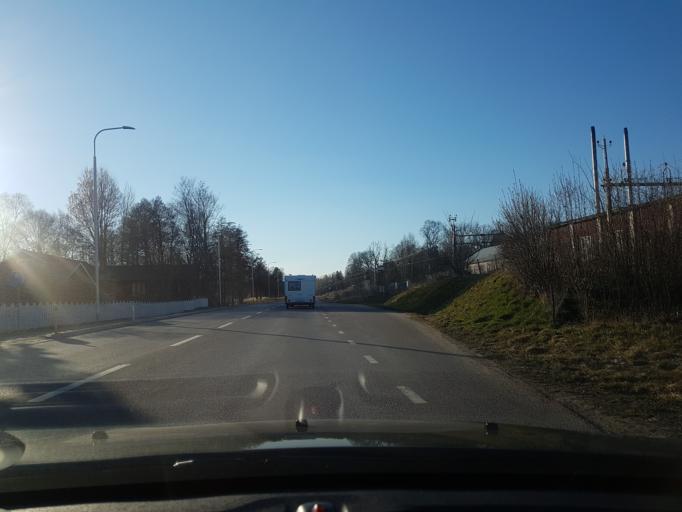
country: SE
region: Uppsala
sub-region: Heby Kommun
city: Morgongava
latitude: 59.9337
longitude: 16.9553
